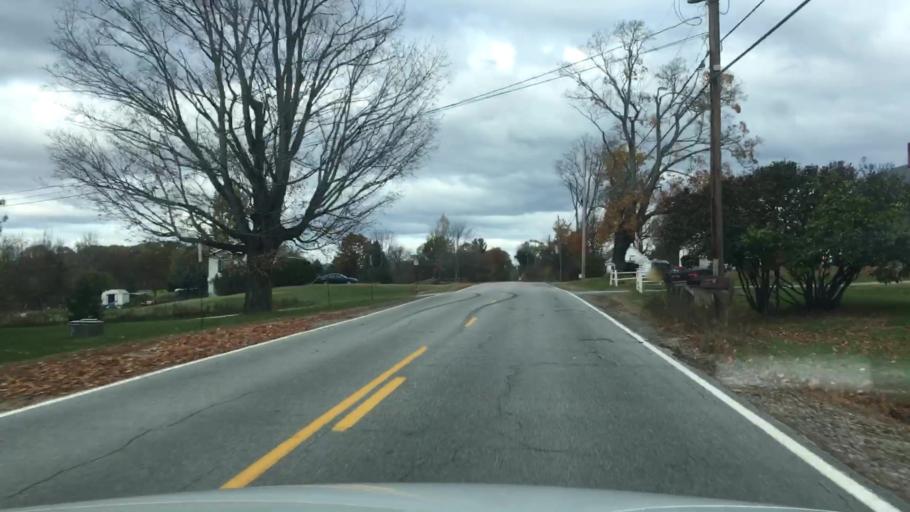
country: US
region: Maine
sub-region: Androscoggin County
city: Sabattus
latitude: 44.1544
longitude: -70.0806
